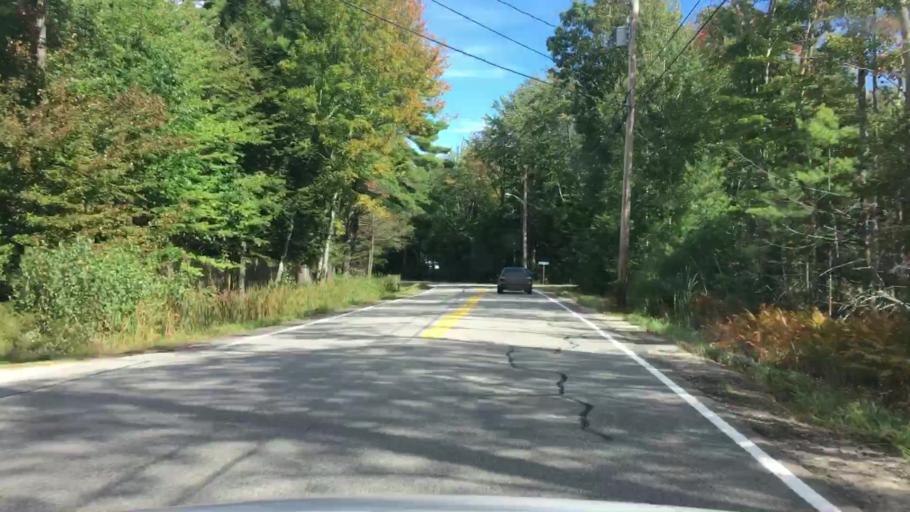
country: US
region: Maine
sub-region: Cumberland County
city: West Scarborough
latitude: 43.5879
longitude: -70.4389
